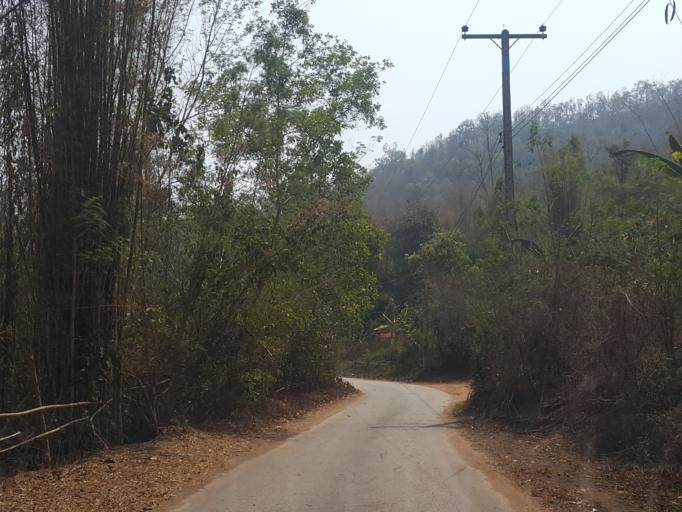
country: TH
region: Chiang Mai
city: Hang Dong
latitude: 18.7369
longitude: 98.8274
